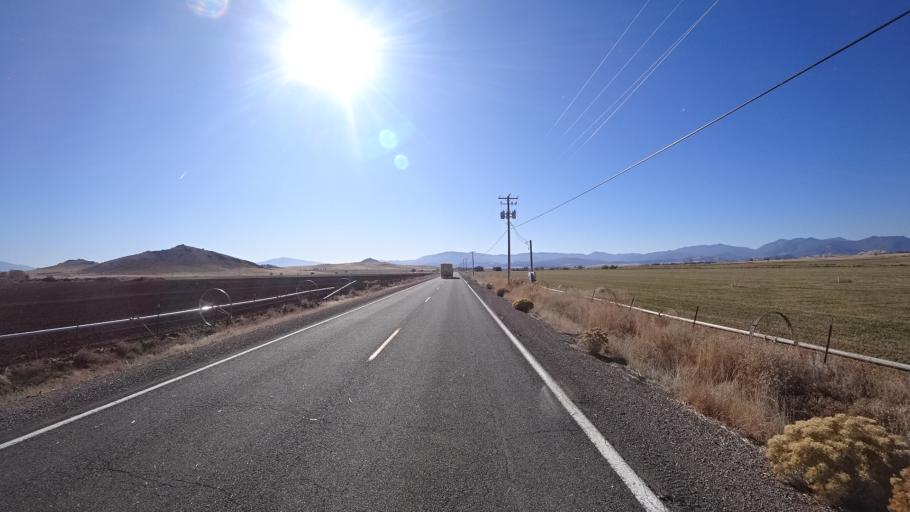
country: US
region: California
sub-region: Siskiyou County
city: Montague
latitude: 41.7614
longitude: -122.4898
